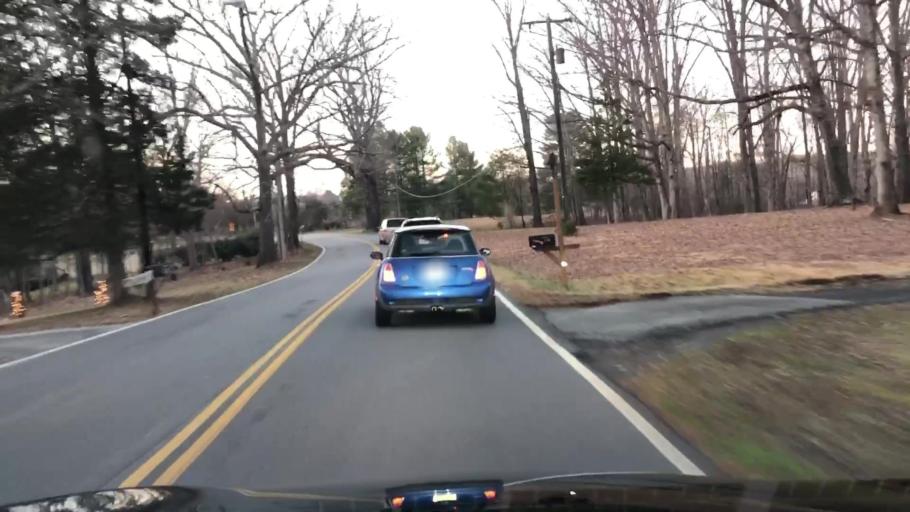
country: US
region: Virginia
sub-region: City of Lynchburg
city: West Lynchburg
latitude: 37.4203
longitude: -79.2434
